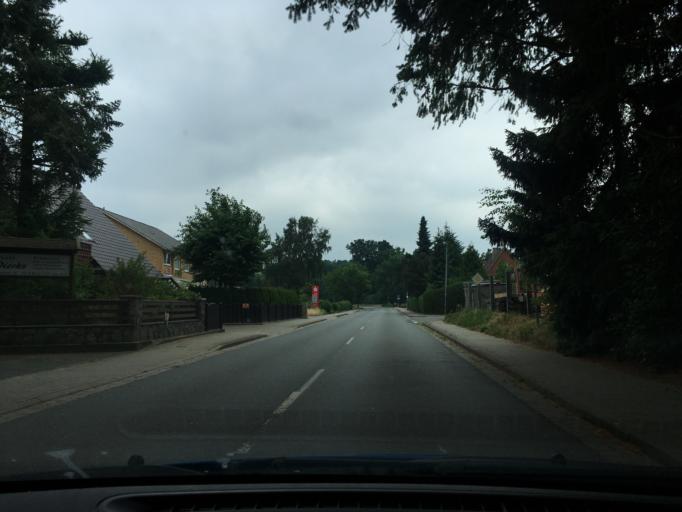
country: DE
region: Lower Saxony
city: Zernien
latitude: 53.0687
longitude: 10.8850
